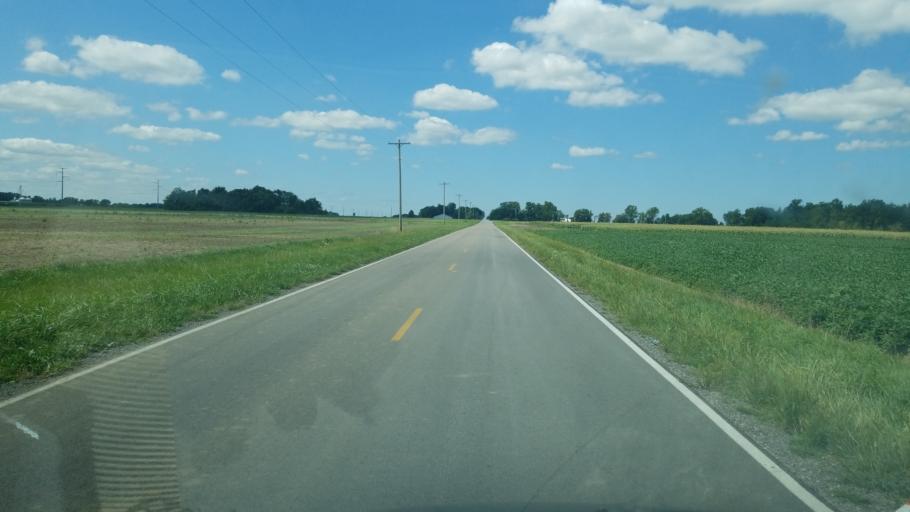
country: US
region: Ohio
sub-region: Fulton County
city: Swanton
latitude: 41.6031
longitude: -83.9418
